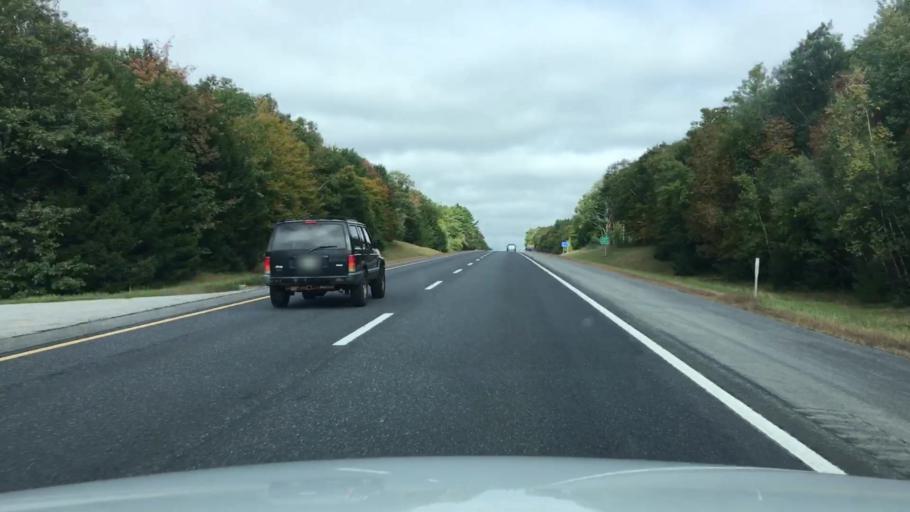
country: US
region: Maine
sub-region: Sagadahoc County
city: Richmond
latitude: 44.1630
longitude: -69.8347
